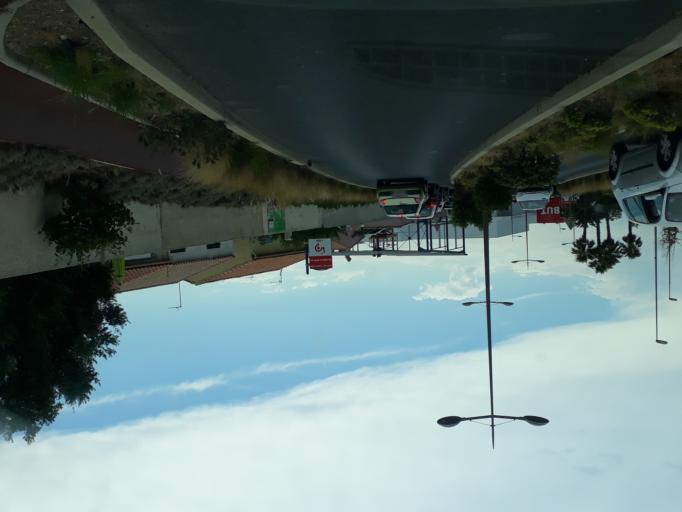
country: FR
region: Languedoc-Roussillon
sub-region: Departement de l'Herault
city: Agde
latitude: 43.3056
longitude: 3.4885
